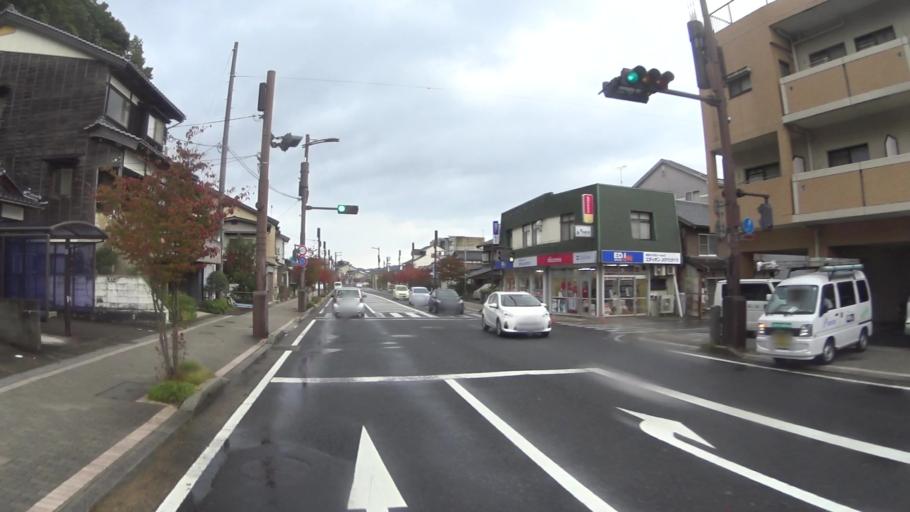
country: JP
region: Kyoto
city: Miyazu
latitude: 35.5309
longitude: 135.1919
